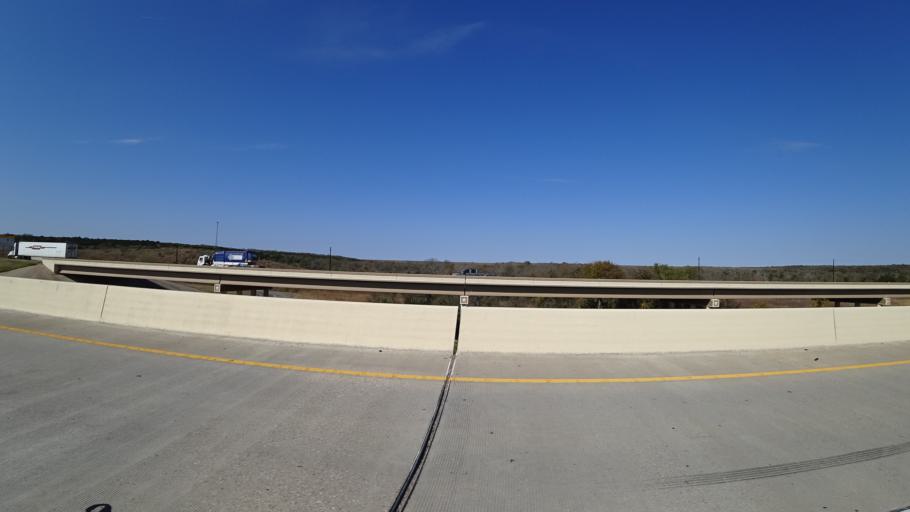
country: US
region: Texas
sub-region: Travis County
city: Hornsby Bend
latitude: 30.2750
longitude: -97.5888
